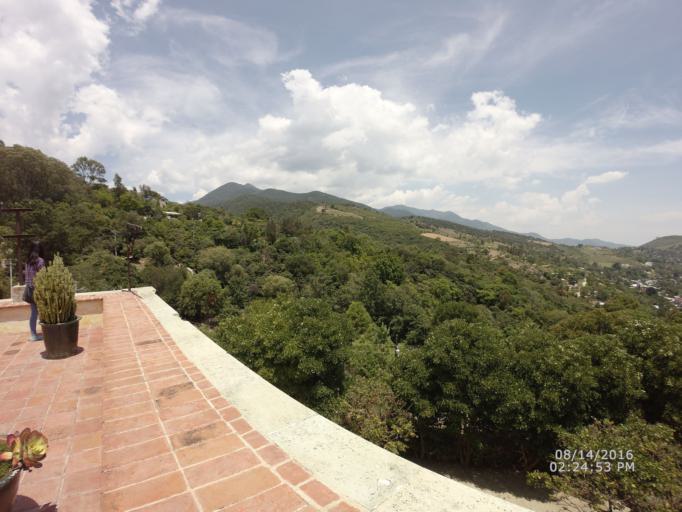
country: MX
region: Oaxaca
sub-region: San Juan Bautista Guelache
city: Fraccionamiento San Miguel
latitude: 17.1970
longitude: -96.7601
